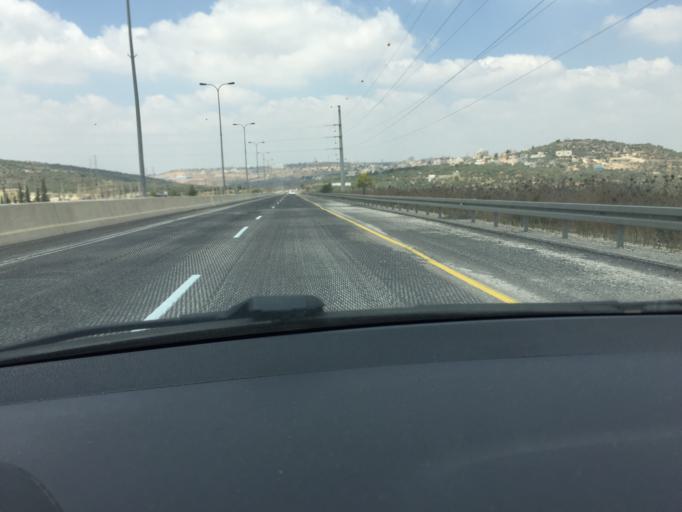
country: PS
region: West Bank
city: Kifil Haris
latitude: 32.1095
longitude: 35.1589
